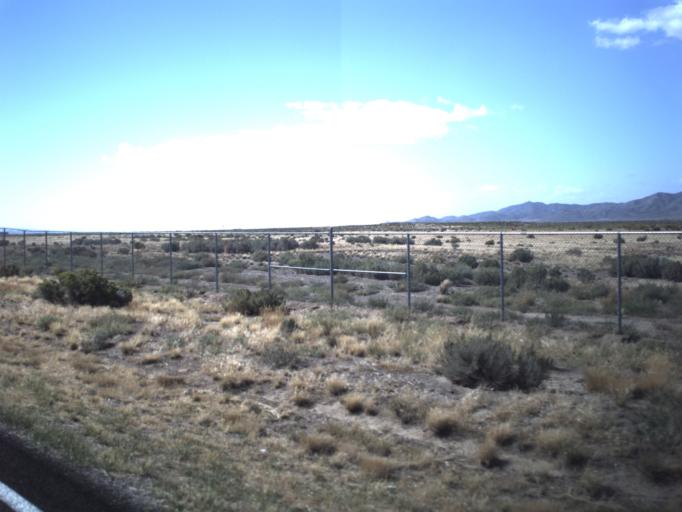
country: US
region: Utah
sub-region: Beaver County
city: Milford
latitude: 38.4300
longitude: -113.0098
